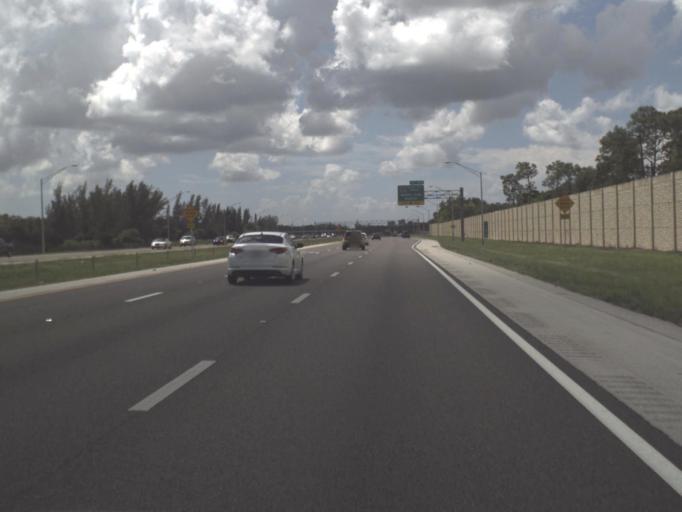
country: US
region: Florida
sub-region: Collier County
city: Golden Gate
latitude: 26.1872
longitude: -81.7359
